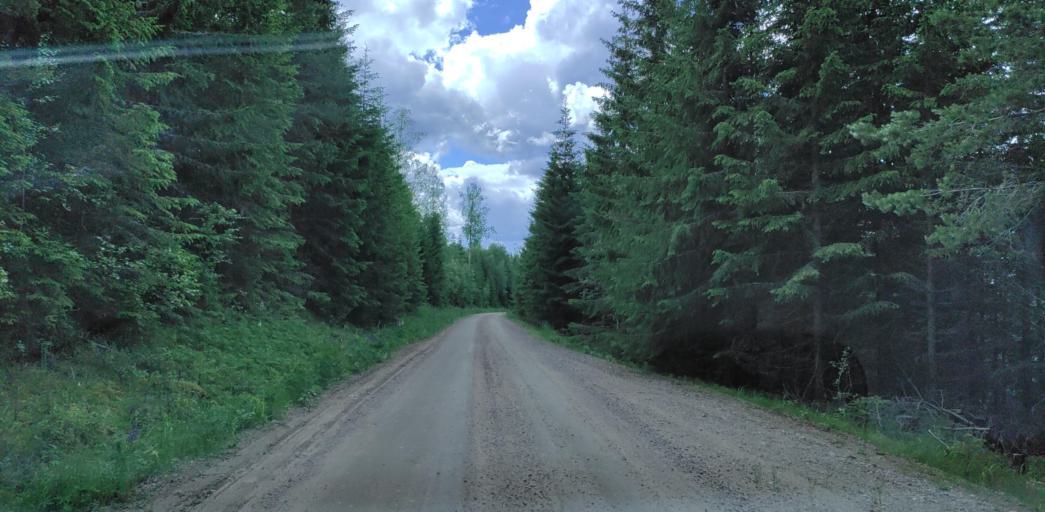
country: SE
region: Vaermland
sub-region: Hagfors Kommun
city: Ekshaerad
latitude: 60.0930
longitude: 13.3434
